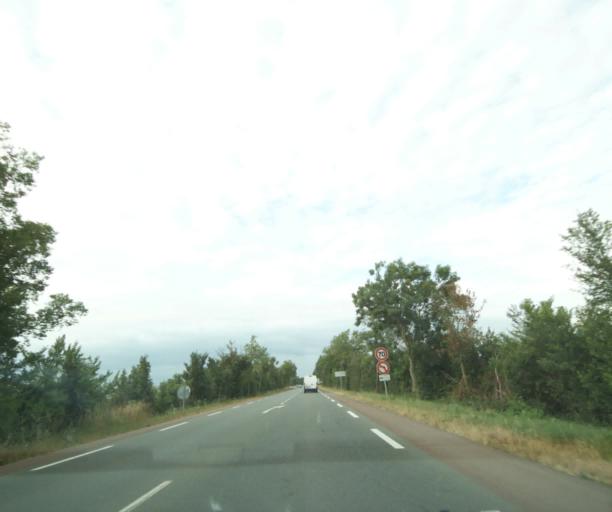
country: FR
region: Poitou-Charentes
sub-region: Departement de la Charente-Maritime
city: Marans
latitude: 46.2816
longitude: -0.9957
